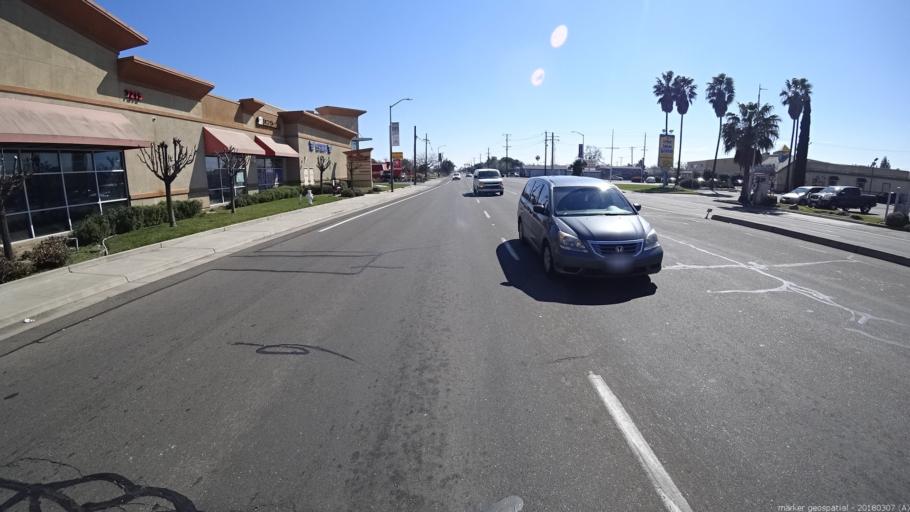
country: US
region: California
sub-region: Sacramento County
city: Florin
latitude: 38.4954
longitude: -121.4287
